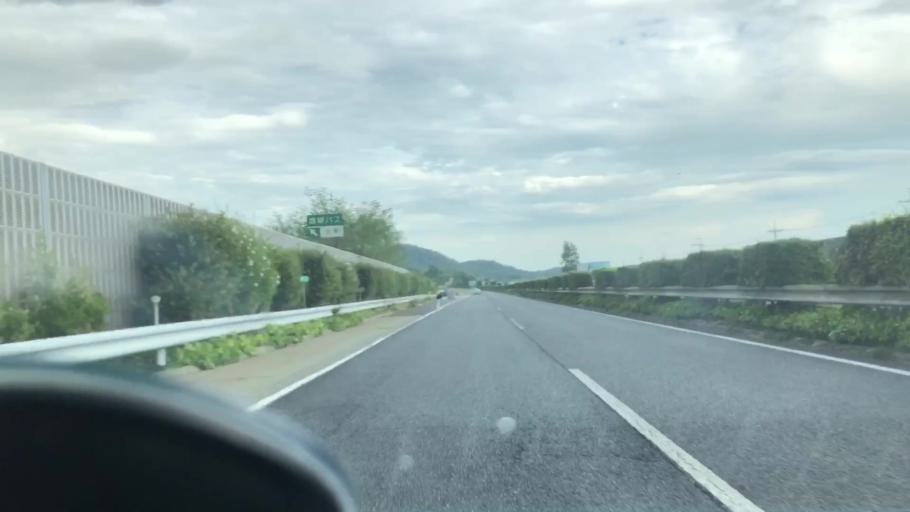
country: JP
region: Hyogo
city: Ono
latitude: 34.9368
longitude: 134.8337
